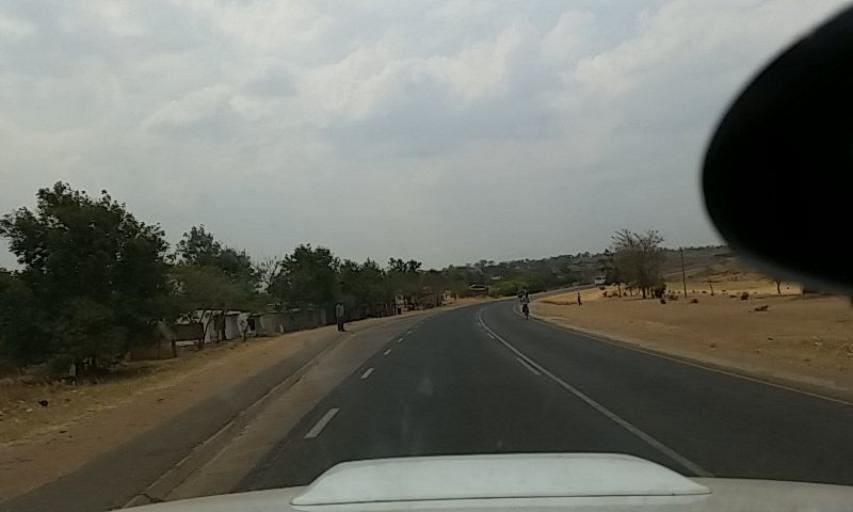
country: MW
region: Central Region
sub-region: Lilongwe District
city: Lilongwe
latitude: -13.8561
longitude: 33.8323
